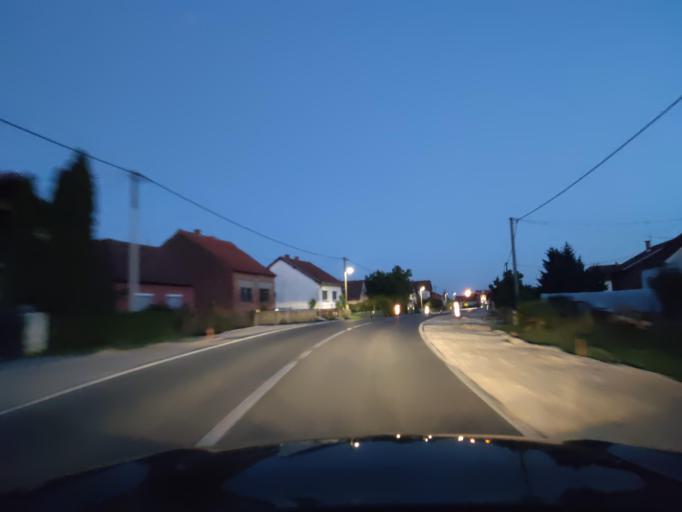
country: HR
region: Medimurska
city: Mackovec
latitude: 46.4496
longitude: 16.4322
